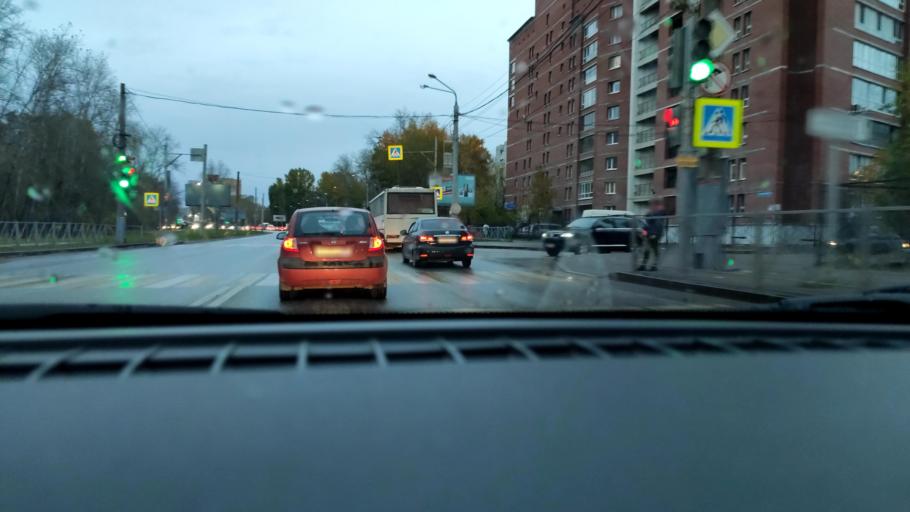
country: RU
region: Perm
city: Kondratovo
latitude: 57.9808
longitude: 56.1715
